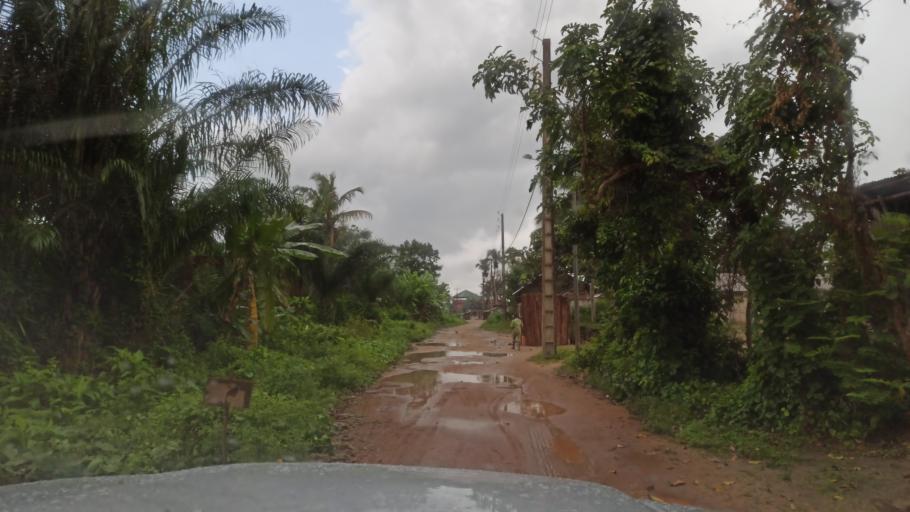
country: BJ
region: Queme
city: Porto-Novo
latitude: 6.4532
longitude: 2.6568
